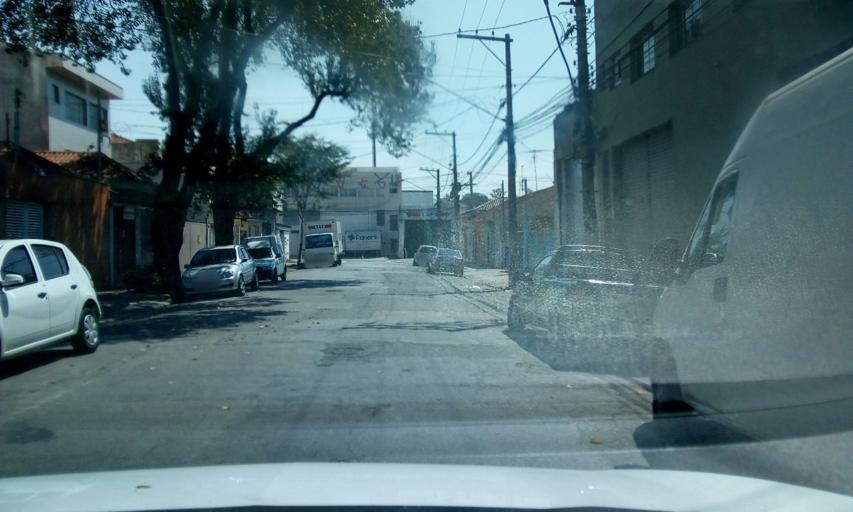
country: BR
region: Sao Paulo
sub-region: Osasco
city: Osasco
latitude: -23.5159
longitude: -46.7220
